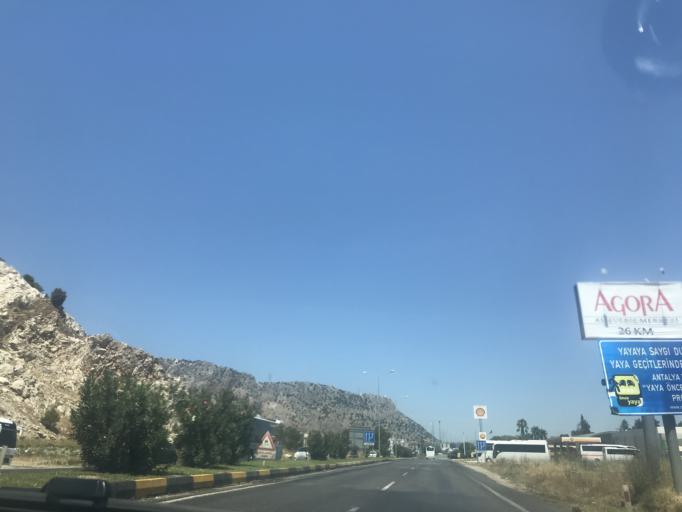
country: TR
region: Antalya
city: Cakirlar
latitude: 36.8317
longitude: 30.5954
